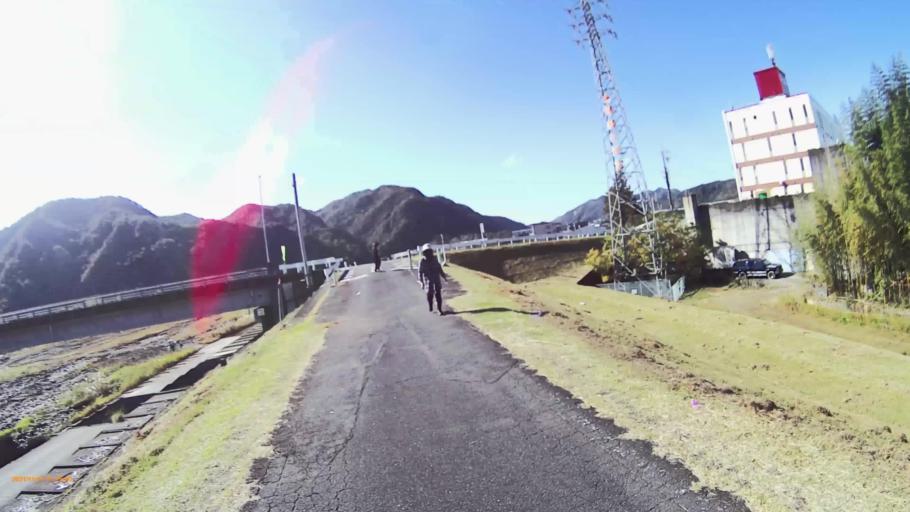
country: JP
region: Gifu
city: Minokamo
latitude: 35.4281
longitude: 137.0007
